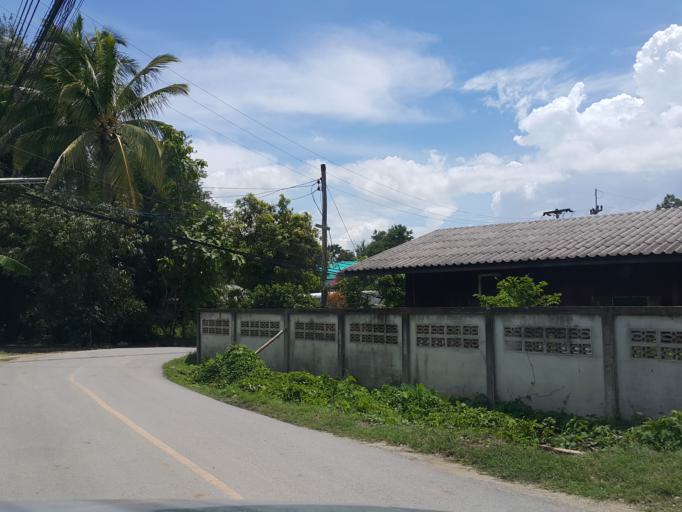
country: TH
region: Chiang Mai
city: San Kamphaeng
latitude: 18.7846
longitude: 99.0923
